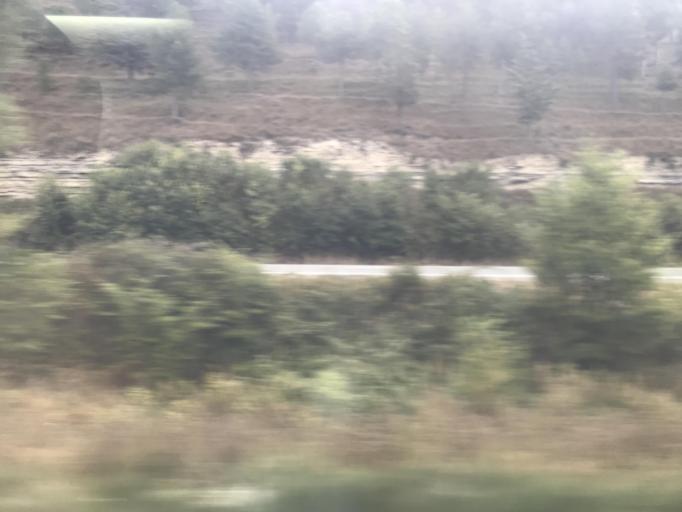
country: ES
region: Castille and Leon
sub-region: Provincia de Burgos
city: Briviesca
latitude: 42.5257
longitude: -3.3307
